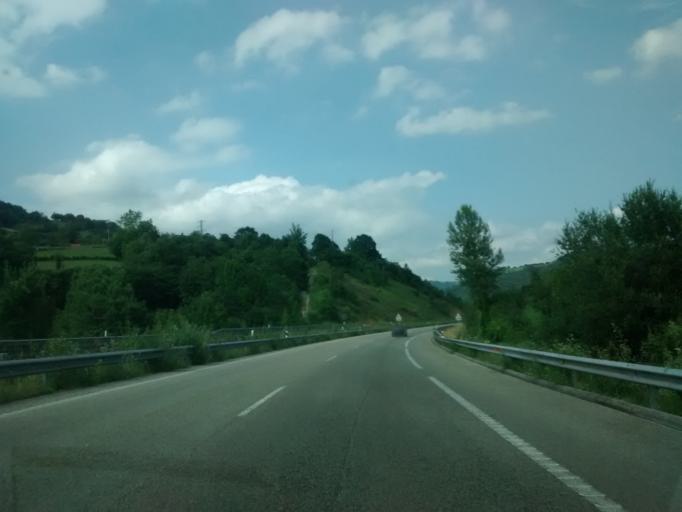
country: ES
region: Asturias
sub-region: Province of Asturias
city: Mieres
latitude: 43.2959
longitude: -5.7562
